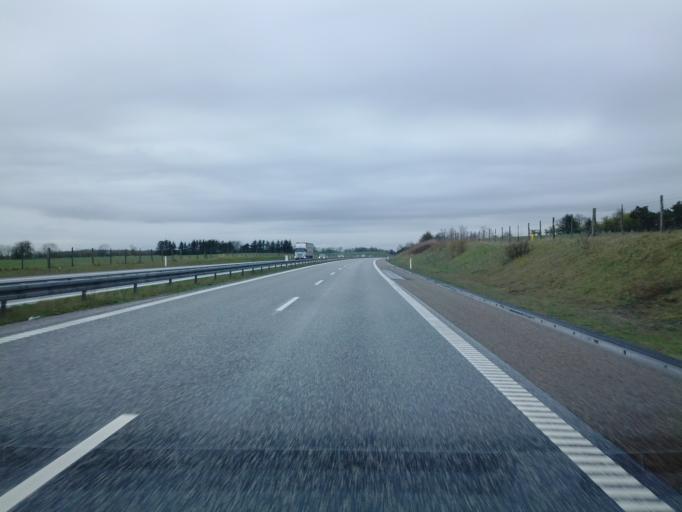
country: DK
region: North Denmark
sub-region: Frederikshavn Kommune
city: Saeby
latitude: 57.2836
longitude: 10.3953
